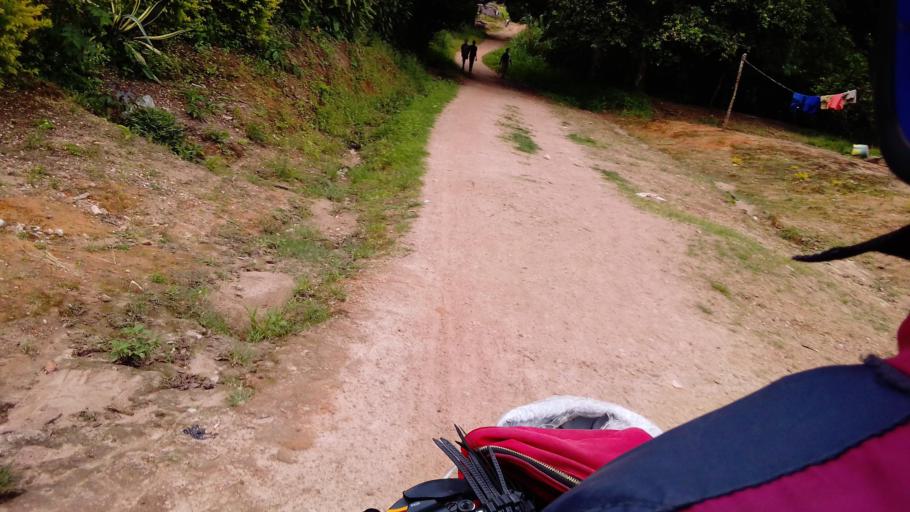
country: SL
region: Eastern Province
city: Koidu
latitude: 8.6753
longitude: -10.9784
